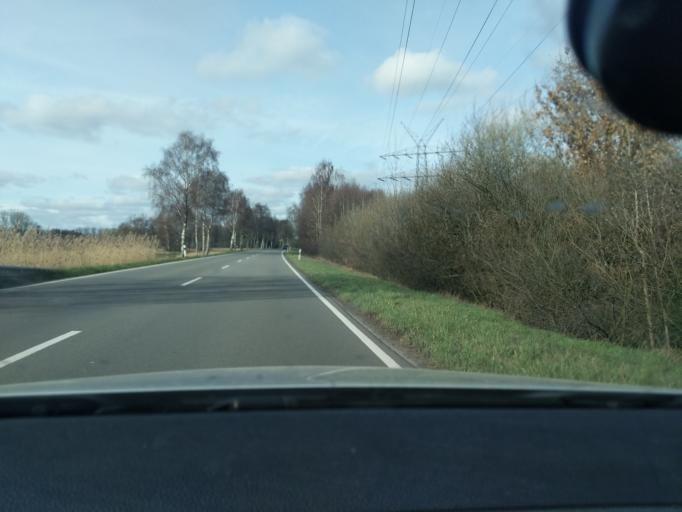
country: DE
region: Lower Saxony
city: Stade
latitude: 53.5869
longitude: 9.5084
